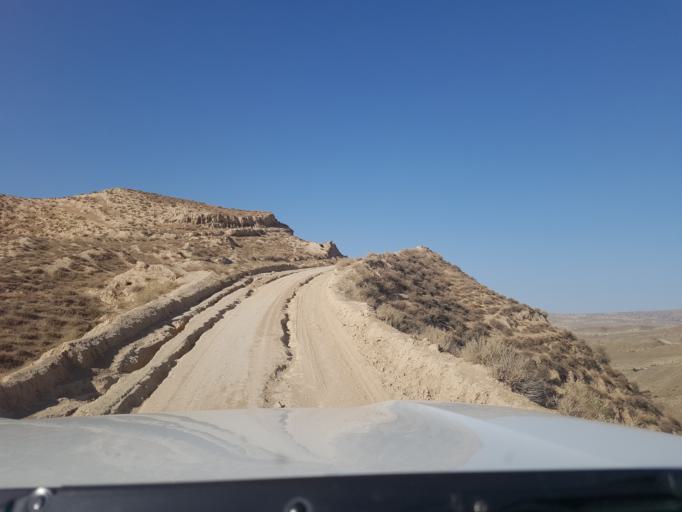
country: TM
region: Balkan
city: Magtymguly
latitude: 38.3035
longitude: 56.7959
